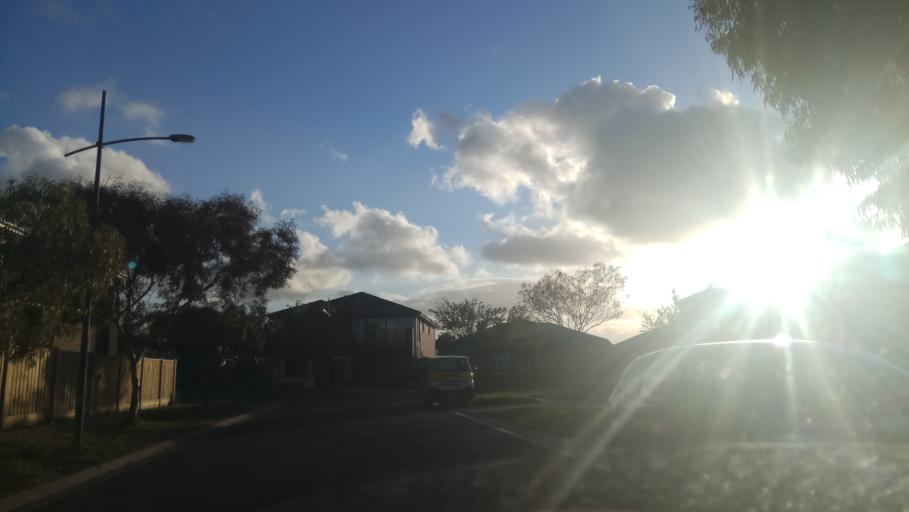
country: AU
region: Victoria
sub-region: Wyndham
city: Point Cook
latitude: -37.9113
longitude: 144.7782
